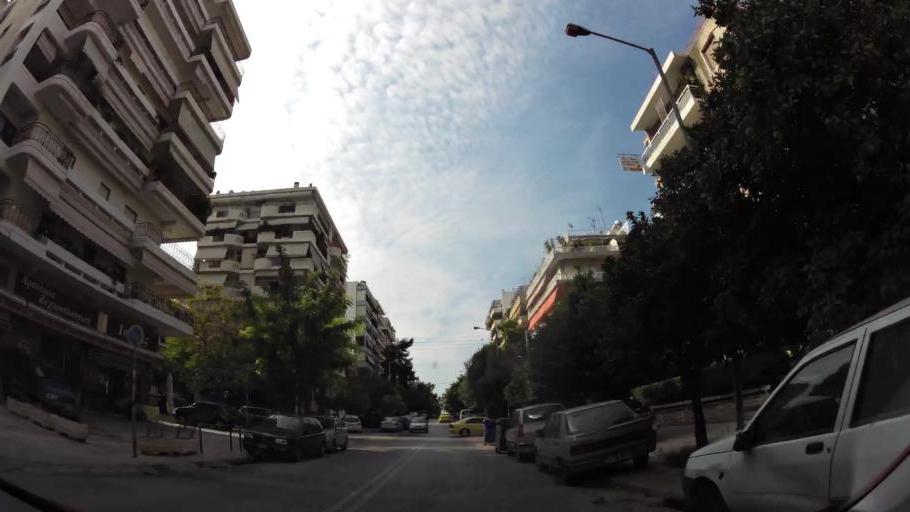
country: GR
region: Attica
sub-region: Nomarchia Athinas
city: Nea Smyrni
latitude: 37.9525
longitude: 23.7131
